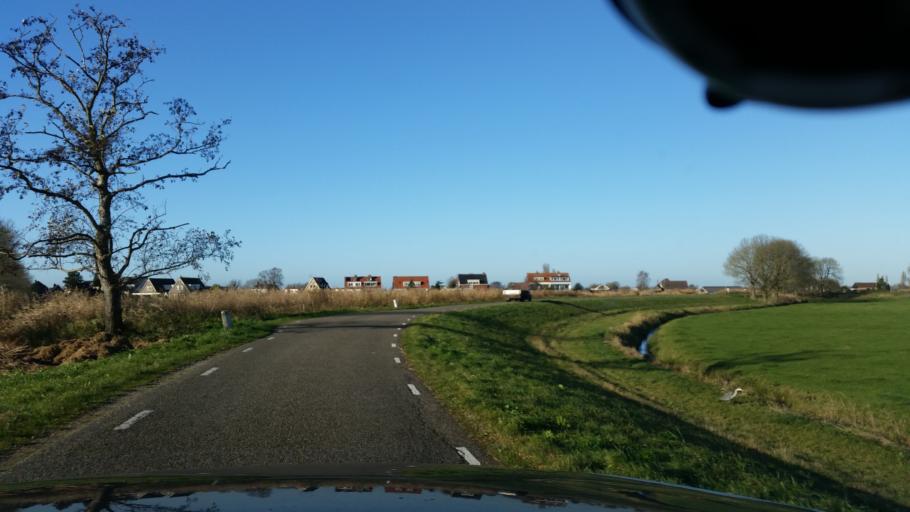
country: NL
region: Utrecht
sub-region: Gemeente De Ronde Venen
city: Mijdrecht
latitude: 52.2510
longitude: 4.8735
